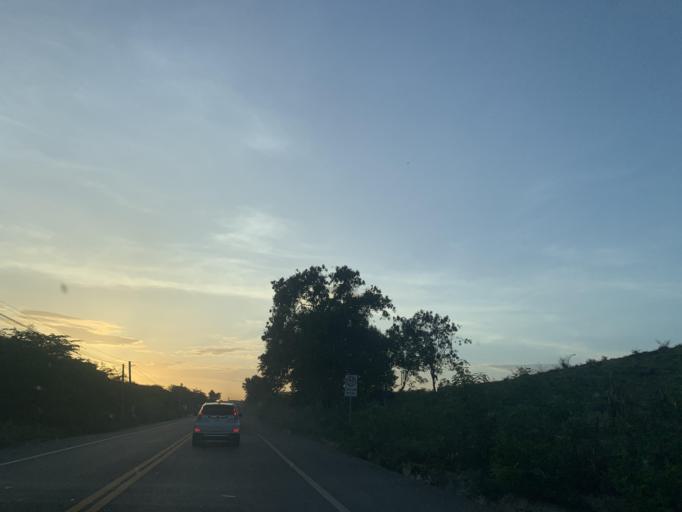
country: DO
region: Puerto Plata
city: Imbert
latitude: 19.7714
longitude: -70.8411
